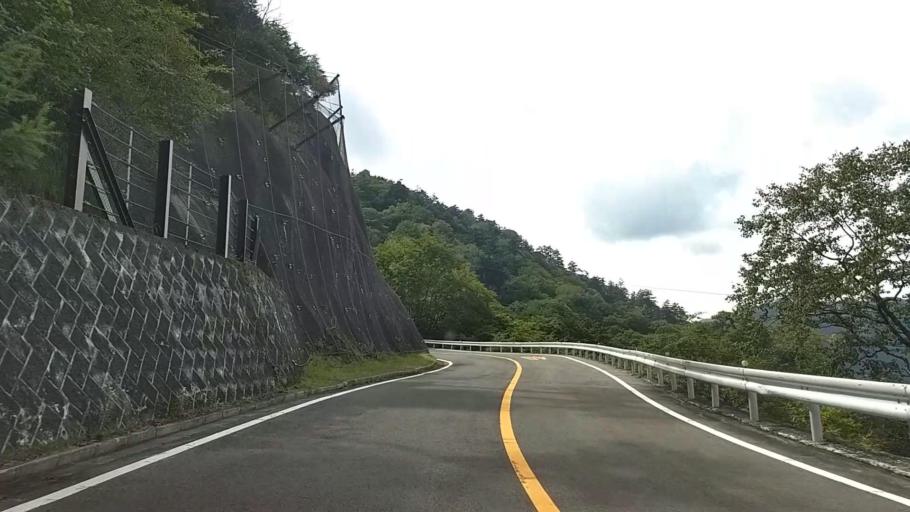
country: JP
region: Tochigi
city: Nikko
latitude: 36.7221
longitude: 139.4947
